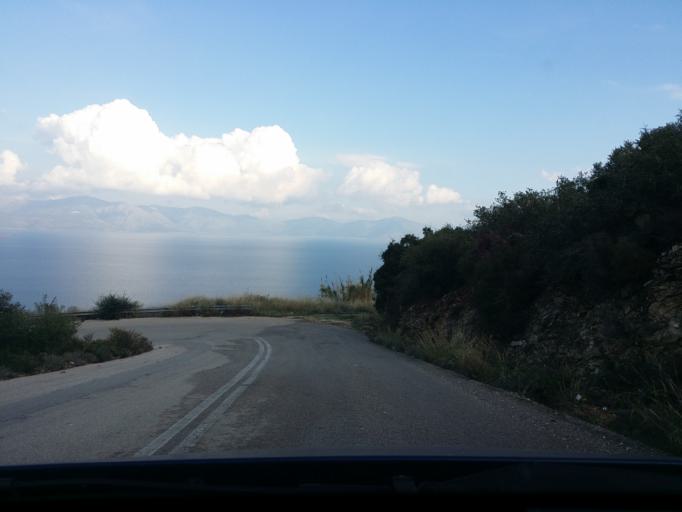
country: GR
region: Attica
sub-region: Nomarchia Anatolikis Attikis
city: Varnavas
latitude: 38.2651
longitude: 23.9675
